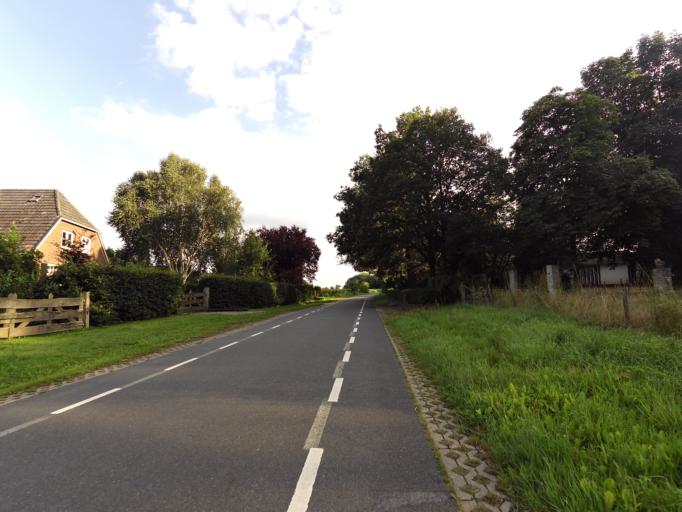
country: NL
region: Gelderland
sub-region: Gemeente Doesburg
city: Doesburg
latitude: 51.9844
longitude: 6.1612
